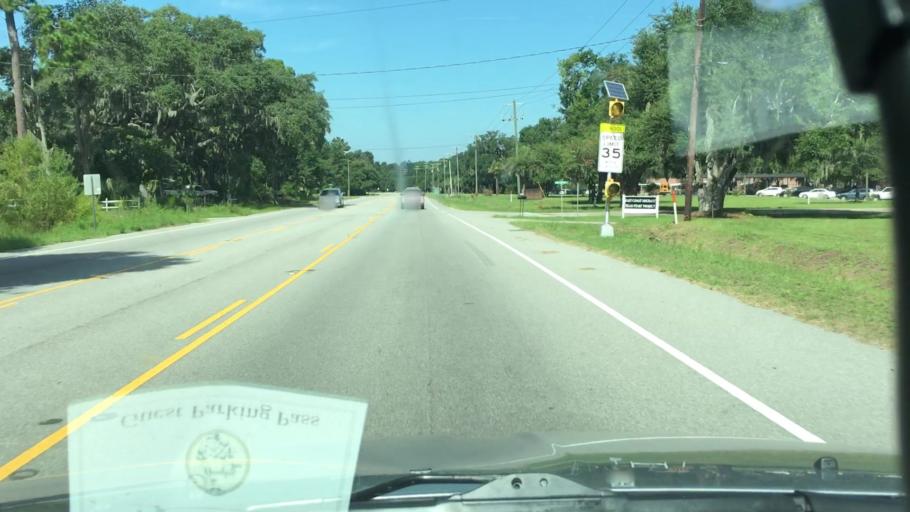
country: US
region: South Carolina
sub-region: Beaufort County
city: Beaufort
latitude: 32.4004
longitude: -80.5602
